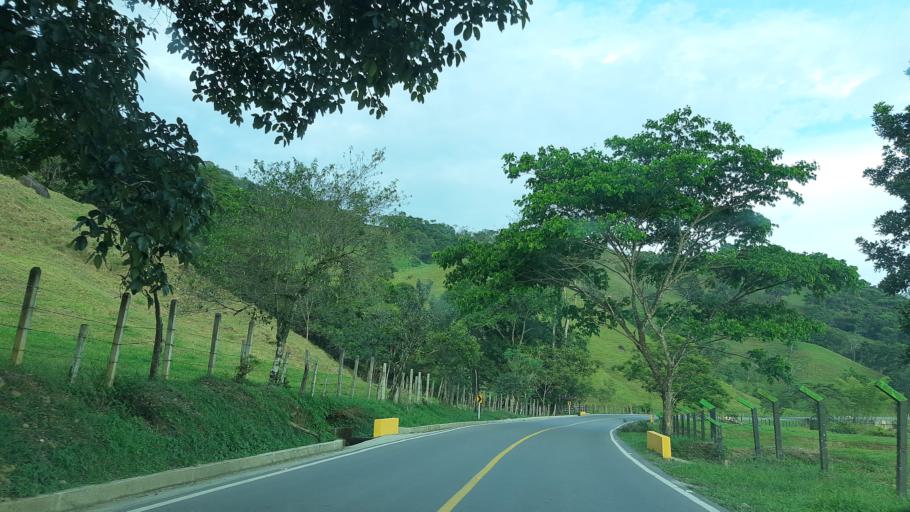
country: CO
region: Boyaca
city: San Luis de Gaceno
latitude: 4.8222
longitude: -73.1933
